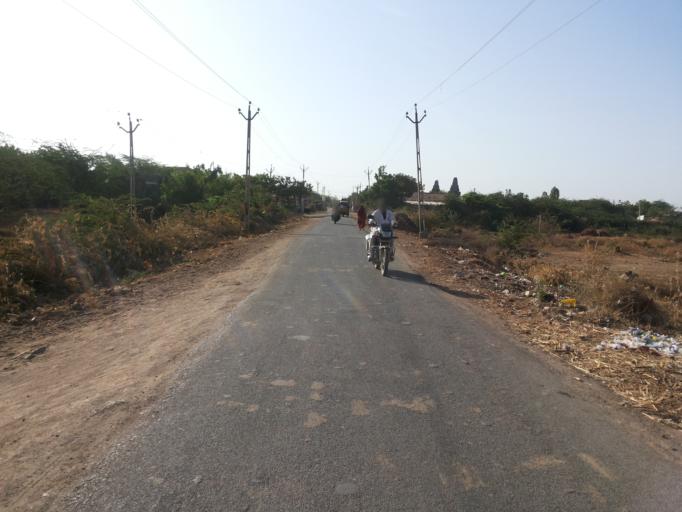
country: IN
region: Gujarat
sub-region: Bhavnagar
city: Katpur
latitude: 21.1069
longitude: 71.8332
